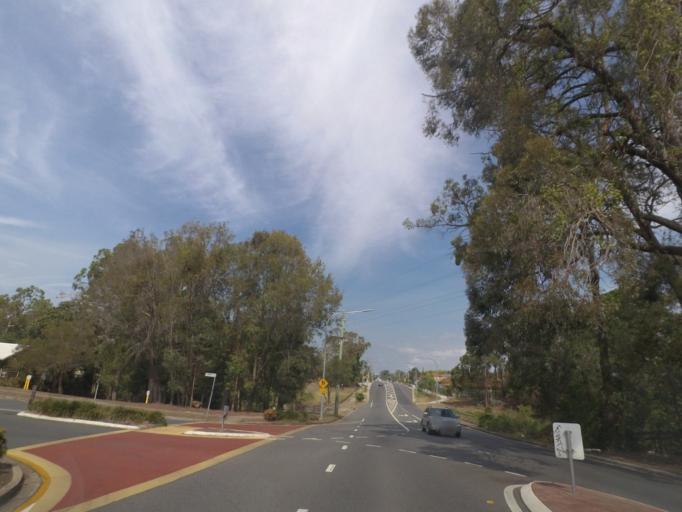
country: AU
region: Queensland
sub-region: Brisbane
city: Sunnybank Hills
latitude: -27.5980
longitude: 153.0488
